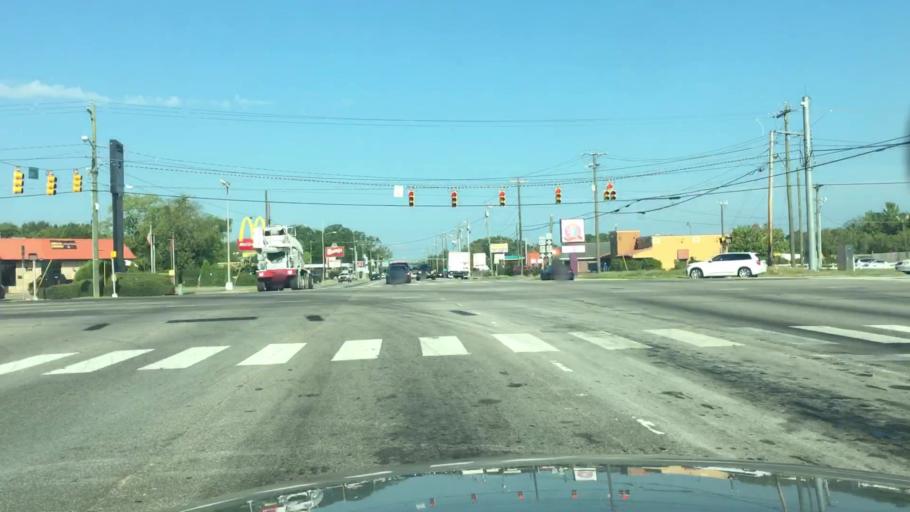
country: US
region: North Carolina
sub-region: Cumberland County
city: Fayetteville
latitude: 35.0527
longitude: -78.8639
